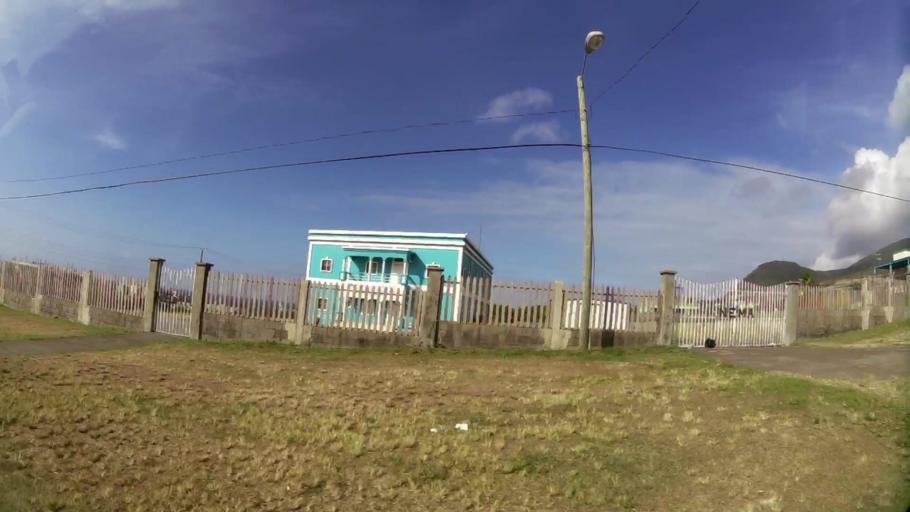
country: KN
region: Saint George Basseterre
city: Basseterre
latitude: 17.2959
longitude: -62.7396
